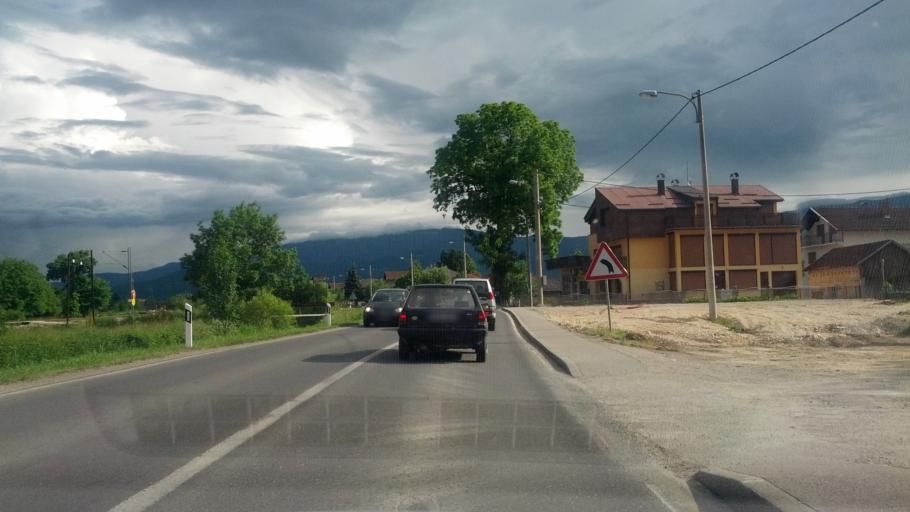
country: BA
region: Federation of Bosnia and Herzegovina
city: Bihac
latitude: 44.8520
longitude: 15.8822
